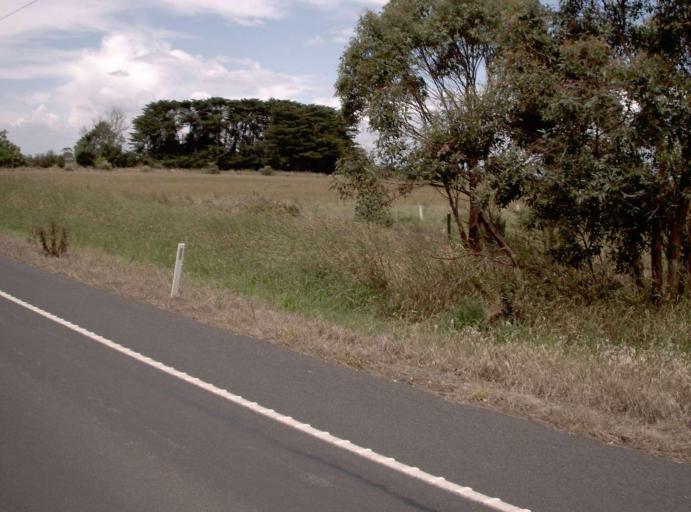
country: AU
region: Victoria
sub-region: Wellington
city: Sale
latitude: -38.0358
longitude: 147.0170
